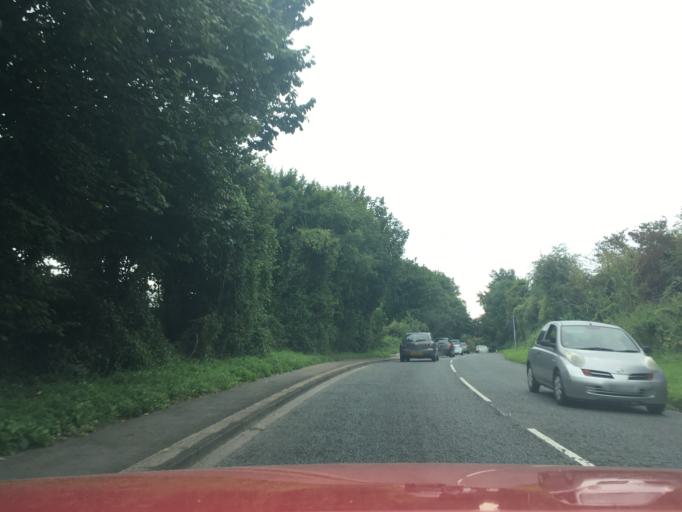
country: GB
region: England
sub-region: South Gloucestershire
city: Alveston
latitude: 51.5958
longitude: -2.5295
